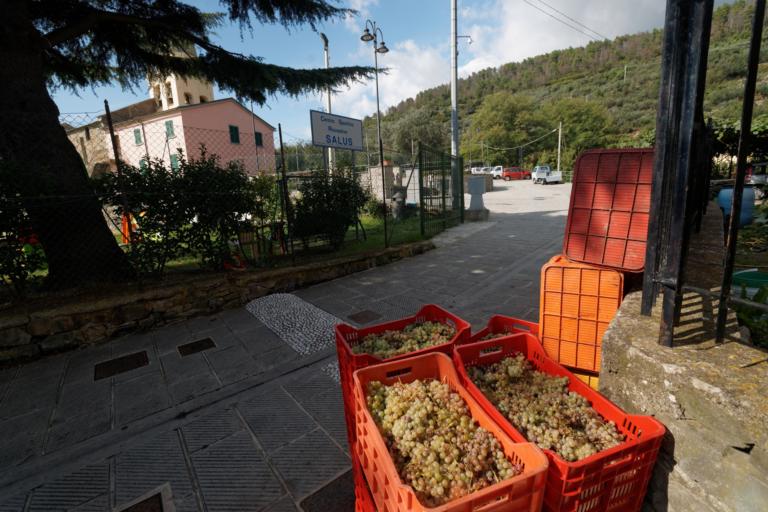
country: IT
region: Liguria
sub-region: Provincia di La Spezia
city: Riomaggiore
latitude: 44.1155
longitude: 9.7302
